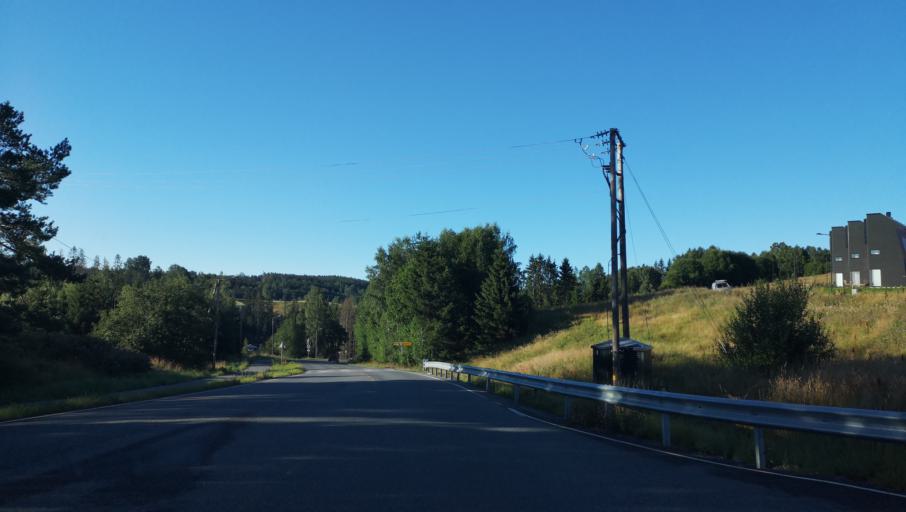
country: NO
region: Ostfold
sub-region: Hobol
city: Tomter
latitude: 59.6574
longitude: 11.0012
